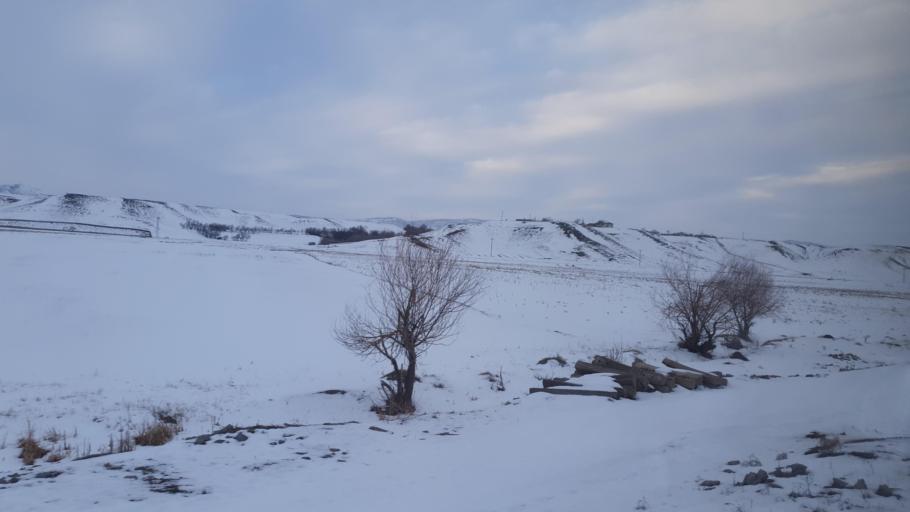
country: TR
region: Kirsehir
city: Mecidiye
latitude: 39.6862
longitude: 34.3966
